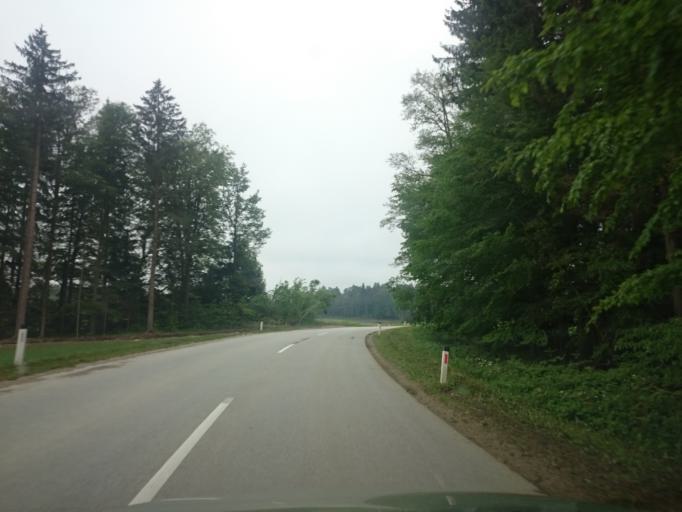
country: SI
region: Sentjur pri Celju
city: Sentjur
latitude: 46.2663
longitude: 15.3934
